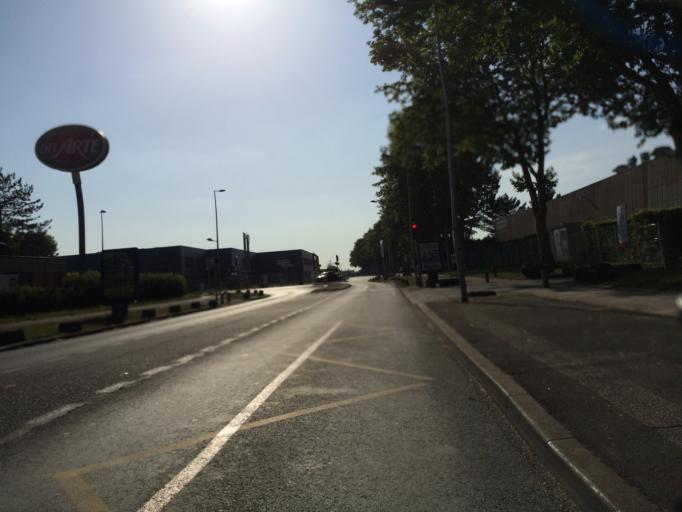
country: FR
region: Ile-de-France
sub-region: Departement de l'Essonne
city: Bondoufle
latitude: 48.6202
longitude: 2.3803
